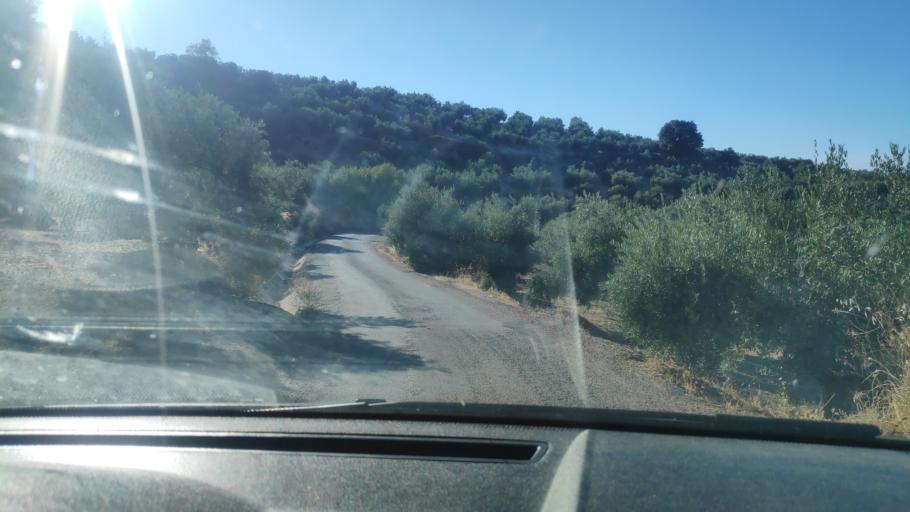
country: ES
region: Andalusia
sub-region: Provincia de Jaen
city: Torres
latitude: 37.7803
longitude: -3.5401
